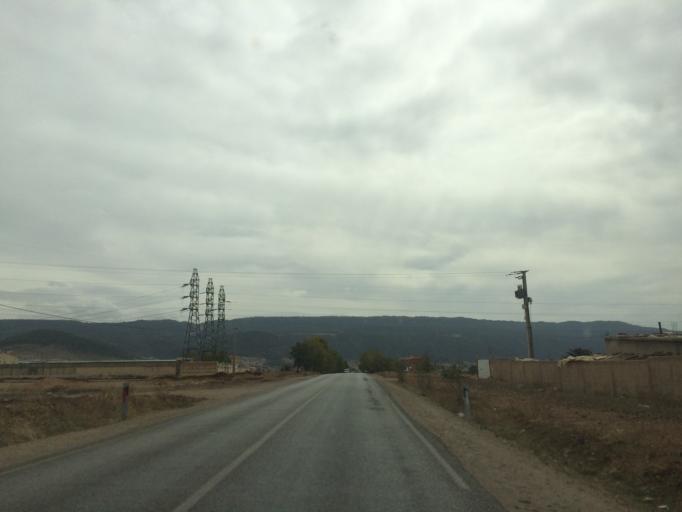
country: MA
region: Meknes-Tafilalet
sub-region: Ifrane
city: Azrou
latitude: 33.4615
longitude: -5.2397
